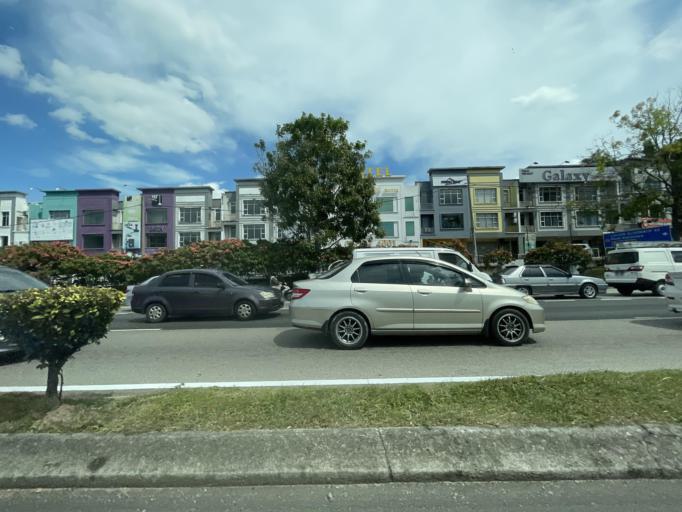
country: MY
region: Melaka
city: Batu Berendam
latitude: 2.2484
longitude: 102.2230
